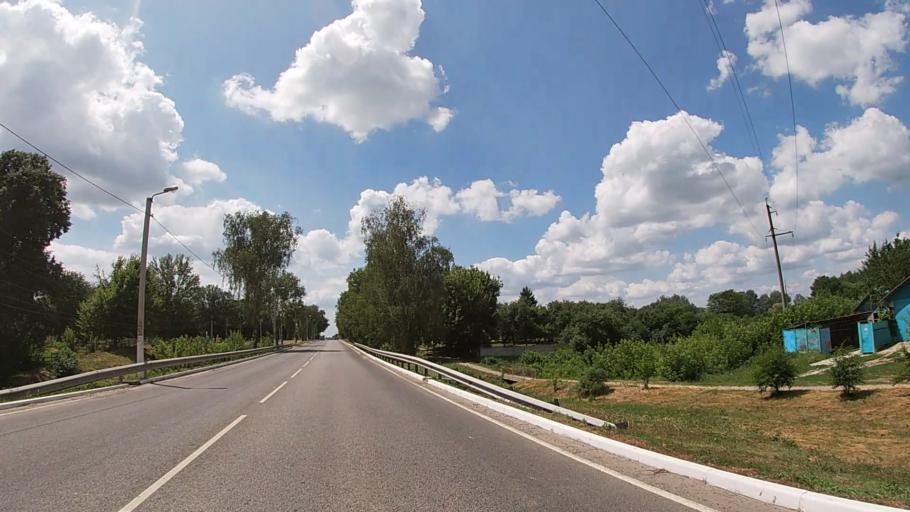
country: RU
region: Belgorod
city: Grayvoron
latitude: 50.4879
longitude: 35.6920
